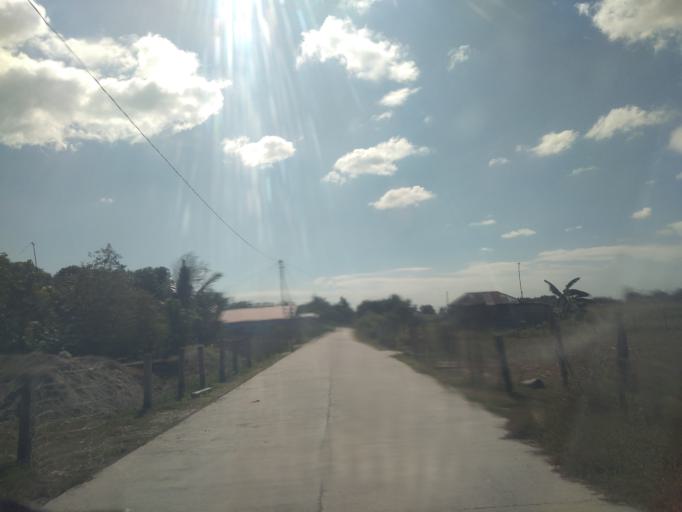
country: PH
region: Central Luzon
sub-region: Province of Pampanga
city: Balas
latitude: 15.0774
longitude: 120.6019
